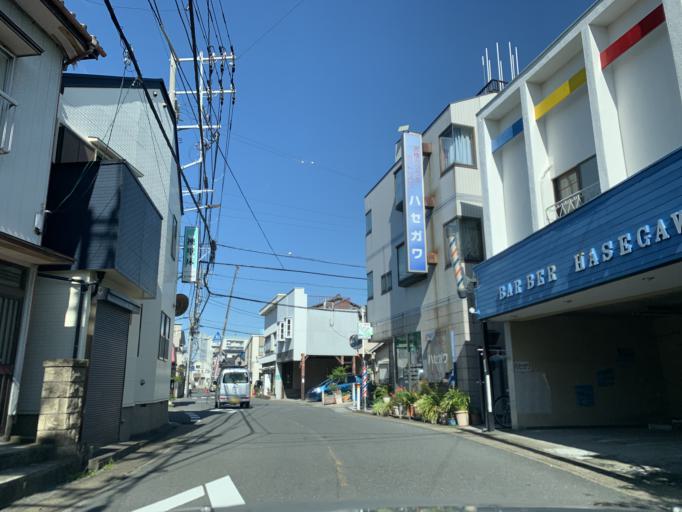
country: JP
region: Tokyo
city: Urayasu
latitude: 35.6789
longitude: 139.8945
